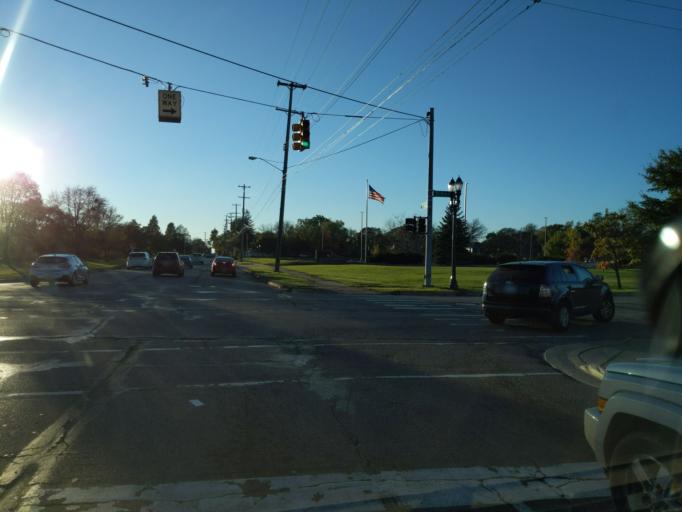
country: US
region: Michigan
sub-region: Ingham County
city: Lansing
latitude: 42.7265
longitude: -84.5671
